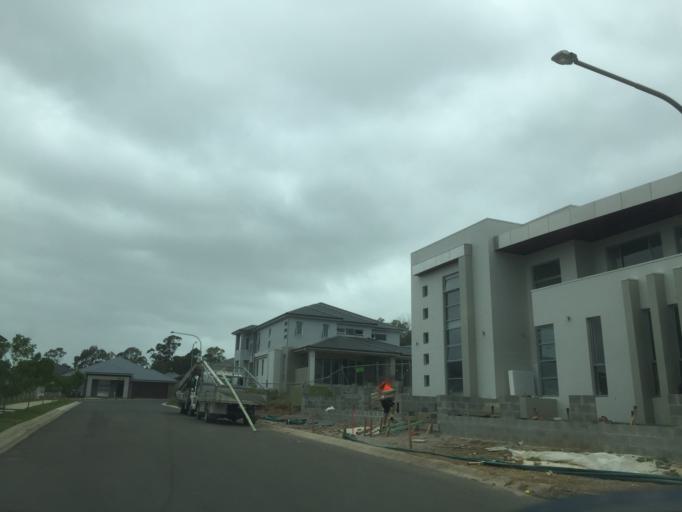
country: AU
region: New South Wales
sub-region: The Hills Shire
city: Beaumont Hills
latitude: -33.7216
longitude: 150.9534
